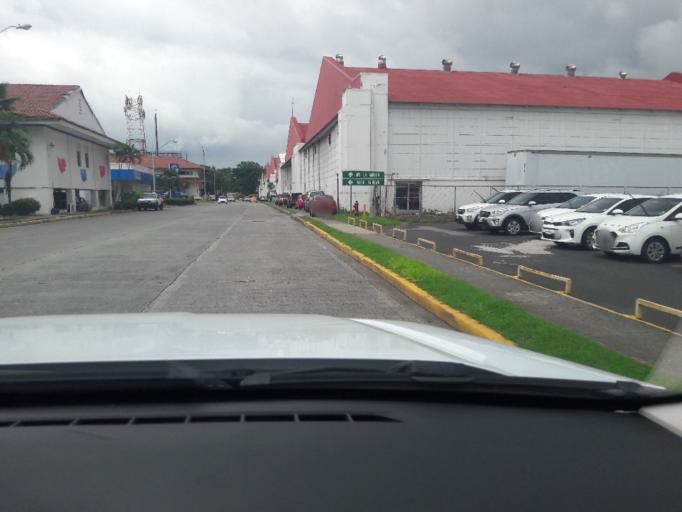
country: PA
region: Panama
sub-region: Distrito de Panama
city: Ancon
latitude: 8.9716
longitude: -79.5597
